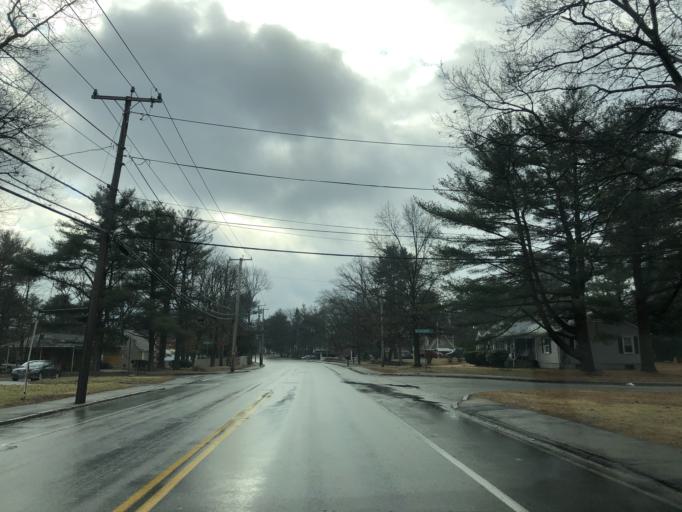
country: US
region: Massachusetts
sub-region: Norfolk County
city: Plainville
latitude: 42.0006
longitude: -71.2957
